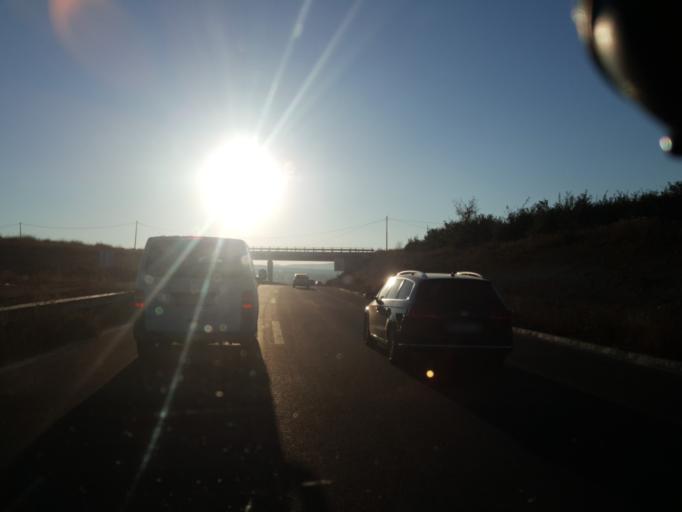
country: XK
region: Prizren
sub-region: Komuna e Malisheves
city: Llazice
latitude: 42.5755
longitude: 20.7201
